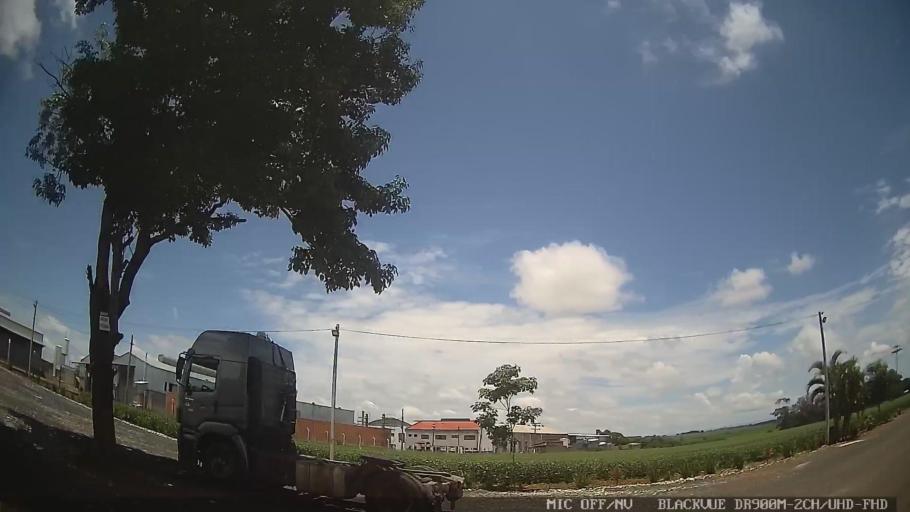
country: BR
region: Sao Paulo
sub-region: Laranjal Paulista
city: Laranjal Paulista
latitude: -23.0330
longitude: -47.8585
